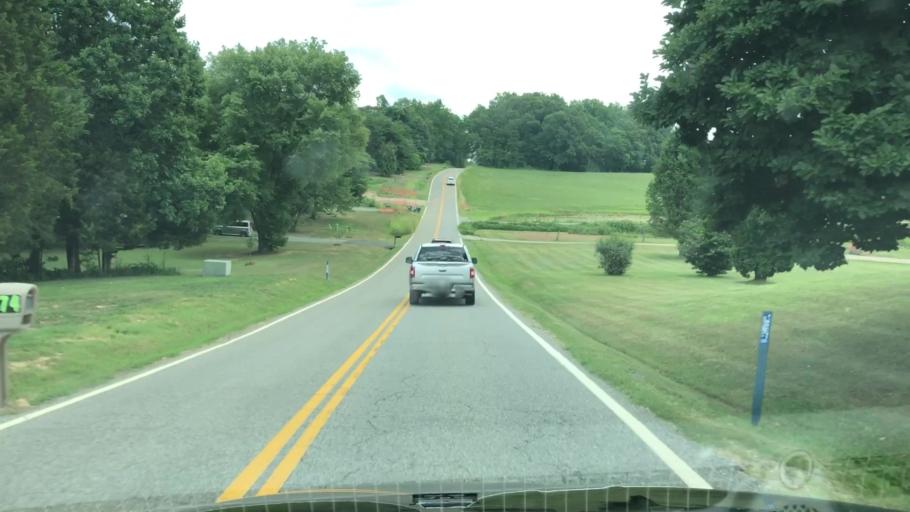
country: US
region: Virginia
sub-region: Stafford County
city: Falmouth
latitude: 38.3418
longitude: -77.5261
